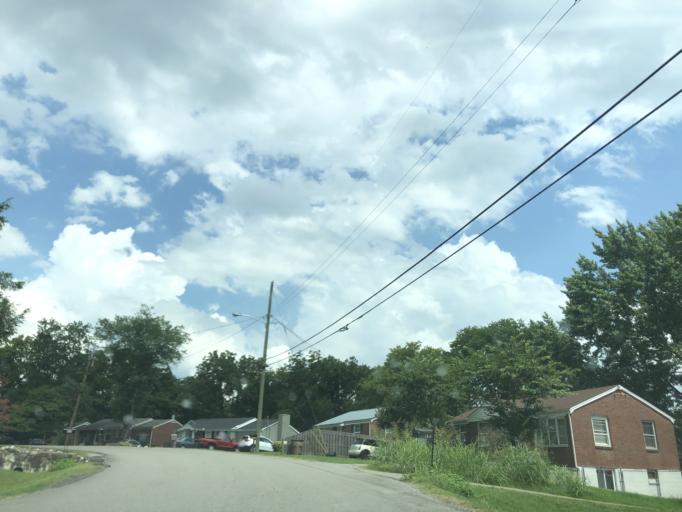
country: US
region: Tennessee
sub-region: Davidson County
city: Lakewood
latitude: 36.1625
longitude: -86.6513
